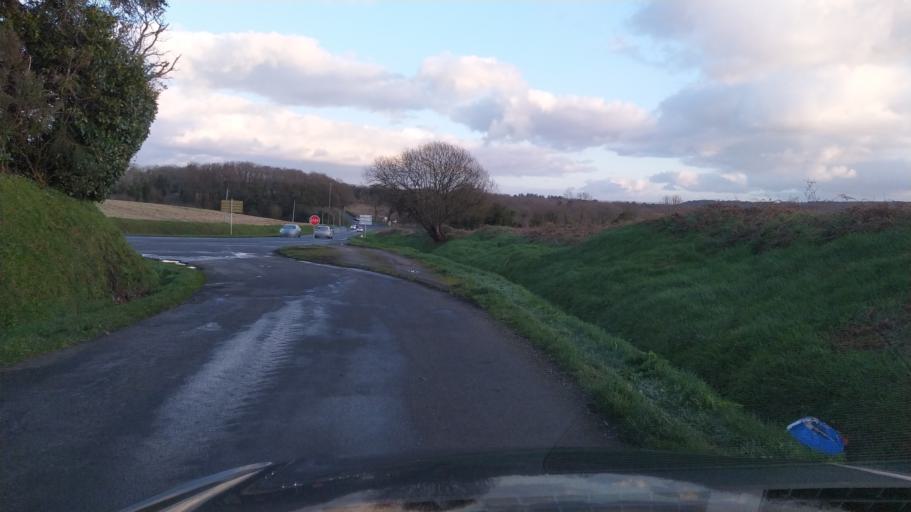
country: FR
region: Brittany
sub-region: Departement du Finistere
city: Bodilis
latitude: 48.5069
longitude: -4.0983
